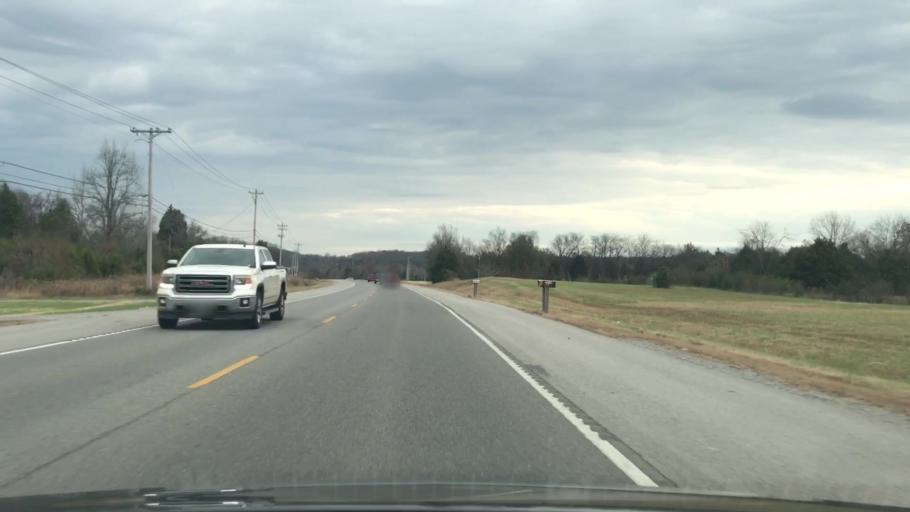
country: US
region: Tennessee
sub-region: Wilson County
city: Lebanon
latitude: 36.2548
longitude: -86.2446
